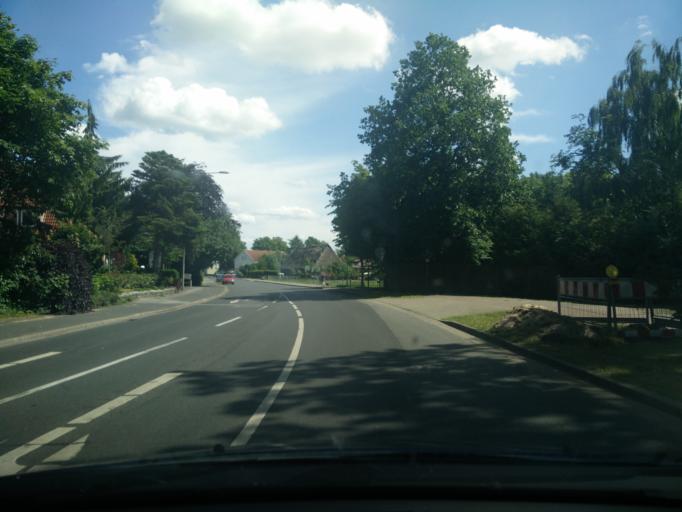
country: DE
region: Schleswig-Holstein
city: Tornesch
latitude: 53.6872
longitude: 9.7257
